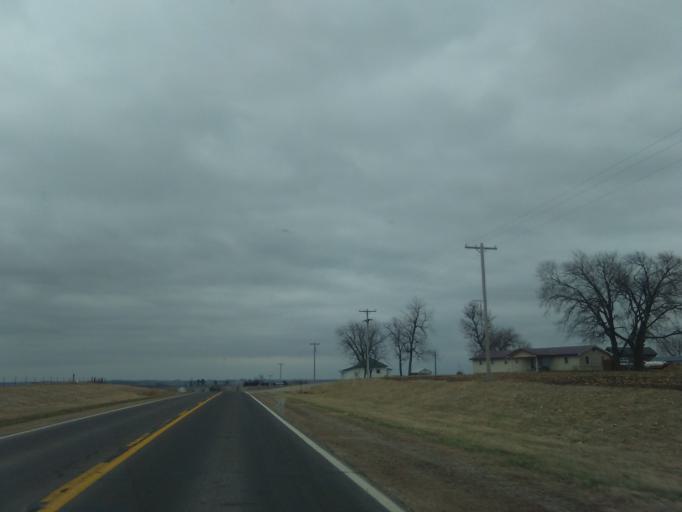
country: US
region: Nebraska
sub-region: Richardson County
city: Falls City
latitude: 40.0583
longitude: -95.5767
